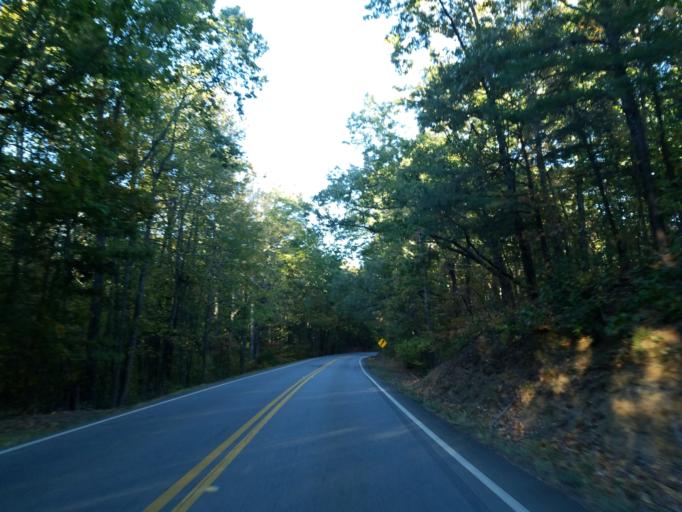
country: US
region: Georgia
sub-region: Dawson County
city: Dawsonville
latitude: 34.4280
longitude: -84.1904
